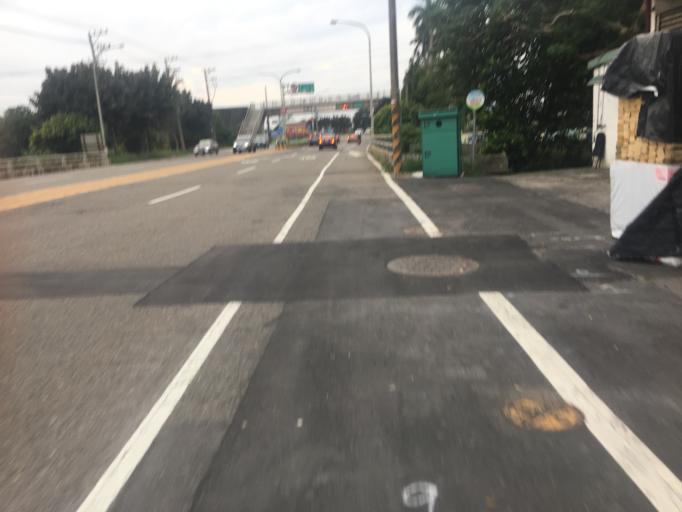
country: TW
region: Taiwan
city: Taoyuan City
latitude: 25.0811
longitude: 121.2159
